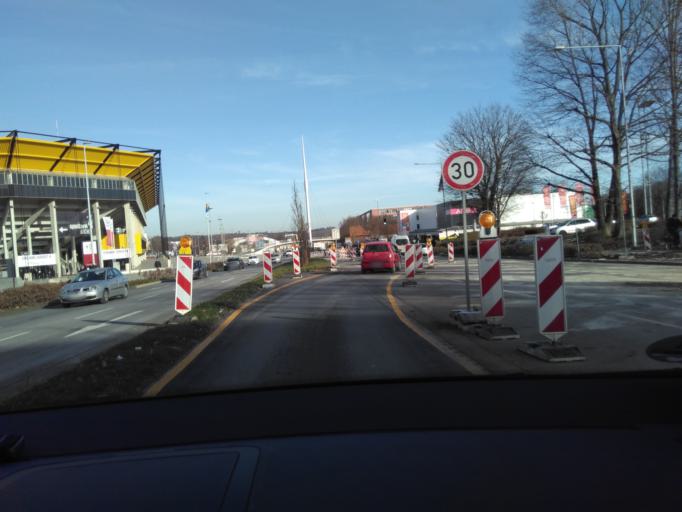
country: DE
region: North Rhine-Westphalia
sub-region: Regierungsbezirk Koln
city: Aachen
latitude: 50.7911
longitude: 6.0975
